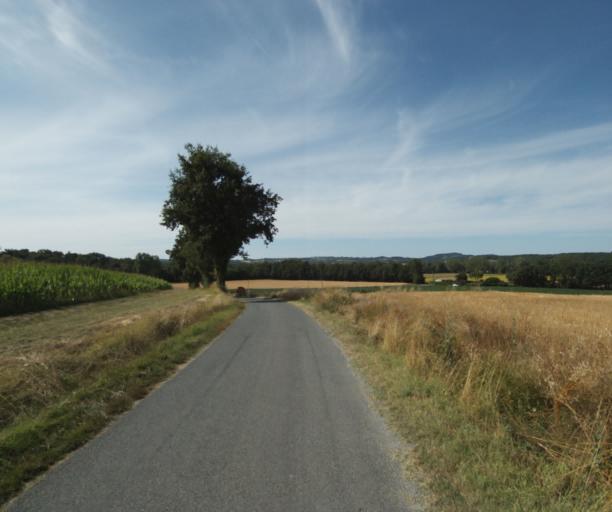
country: FR
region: Midi-Pyrenees
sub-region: Departement du Tarn
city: Soreze
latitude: 43.5108
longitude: 2.0437
